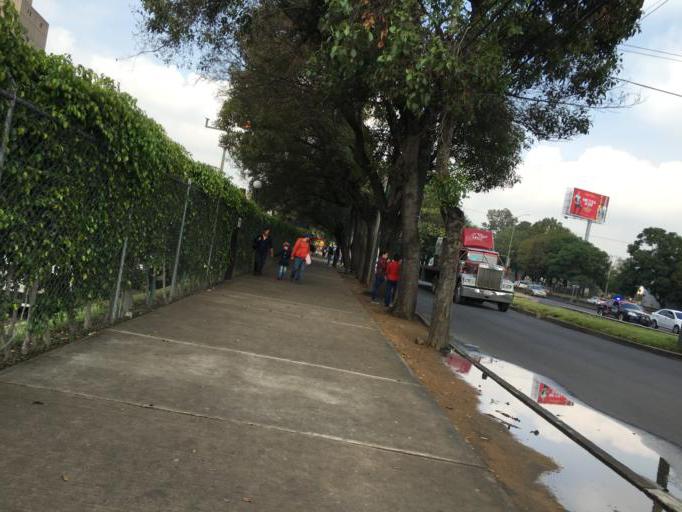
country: MX
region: Mexico City
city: Tlalpan
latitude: 19.2823
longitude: -99.1416
